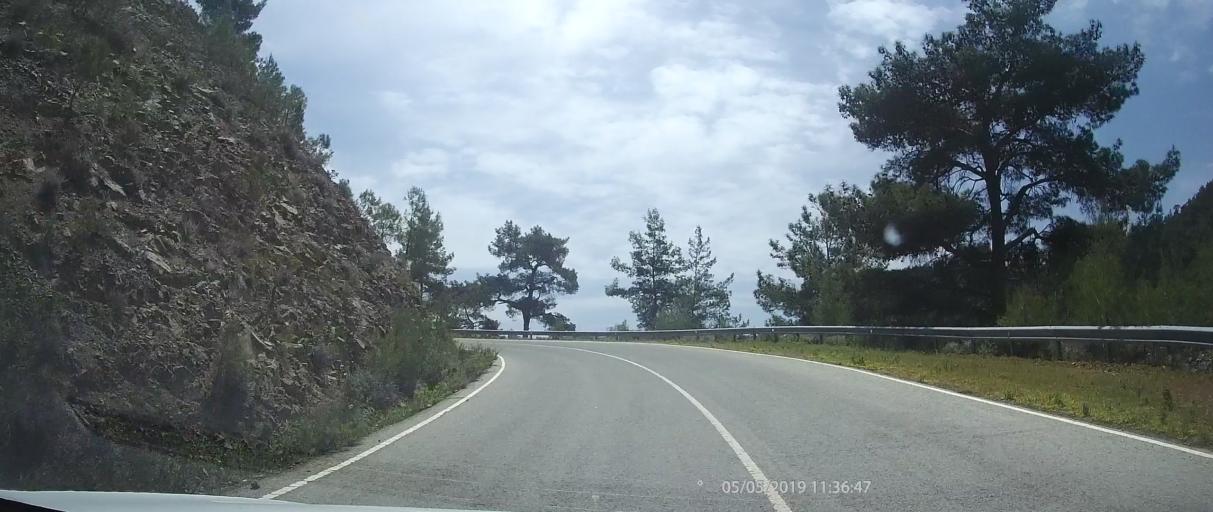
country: CY
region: Lefkosia
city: Kato Pyrgos
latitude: 34.9730
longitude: 32.6543
